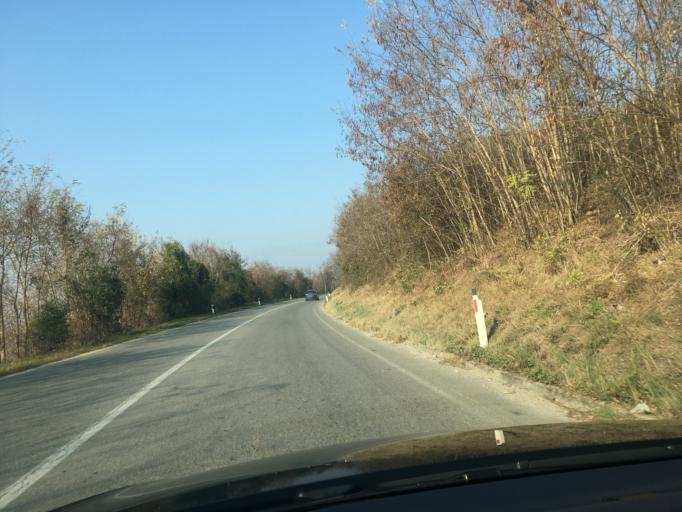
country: XK
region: Pec
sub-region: Komuna e Pejes
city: Dubova (Driloni)
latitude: 42.6439
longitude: 20.4147
